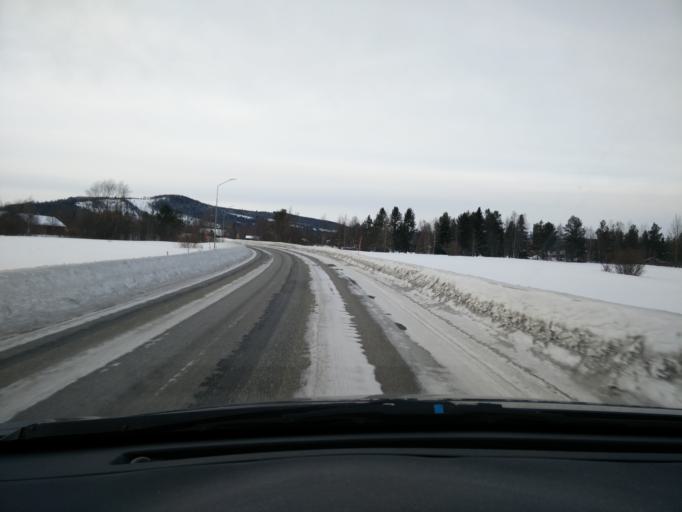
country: SE
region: Jaemtland
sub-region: Harjedalens Kommun
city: Sveg
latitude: 62.4425
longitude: 13.8763
